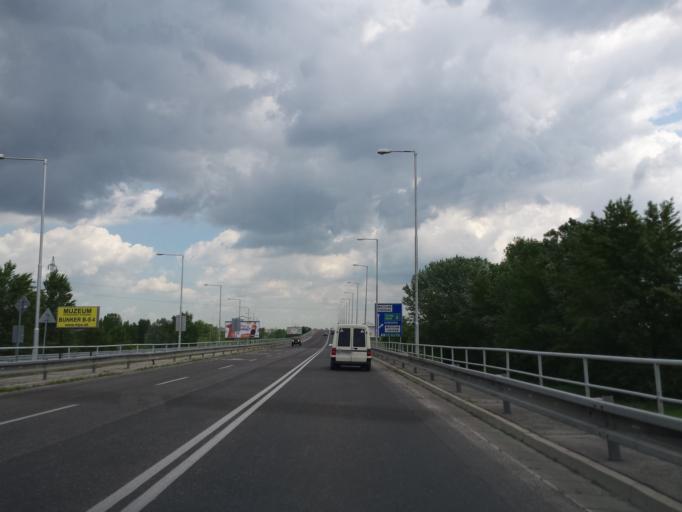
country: AT
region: Burgenland
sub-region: Politischer Bezirk Neusiedl am See
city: Kittsee
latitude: 48.1230
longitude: 17.0703
